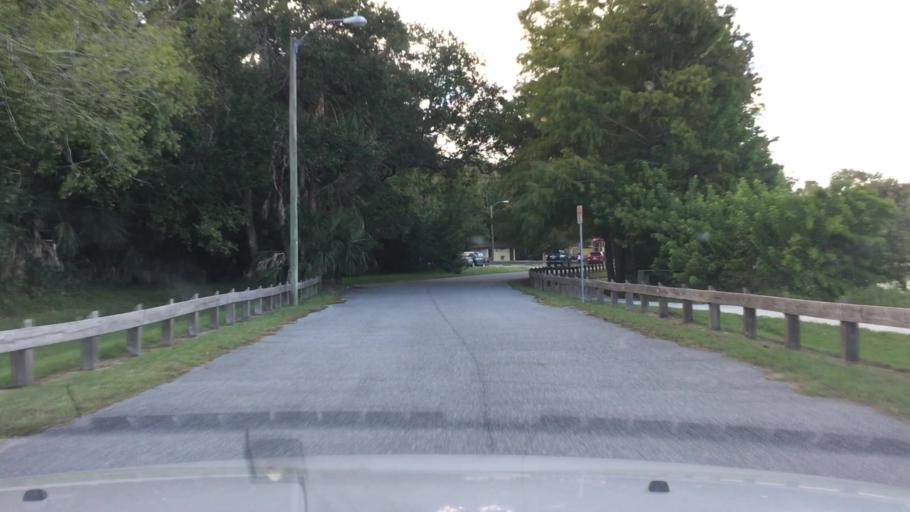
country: US
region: Florida
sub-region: Volusia County
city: Ormond Beach
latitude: 29.2650
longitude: -81.0659
